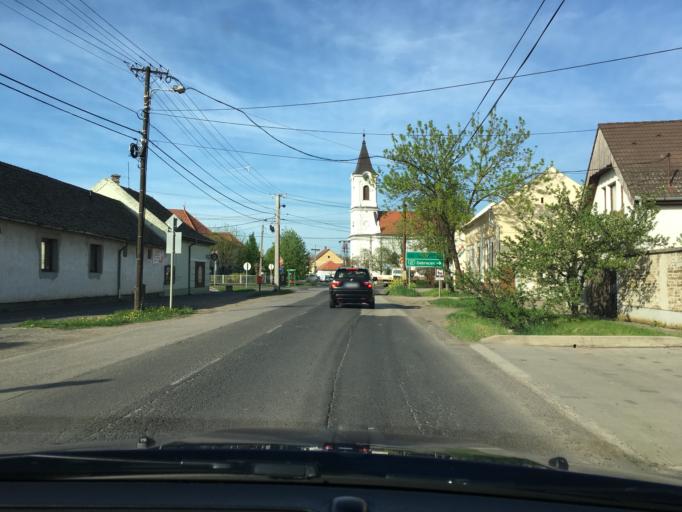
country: HU
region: Bekes
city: Mezobereny
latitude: 46.8168
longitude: 21.0220
